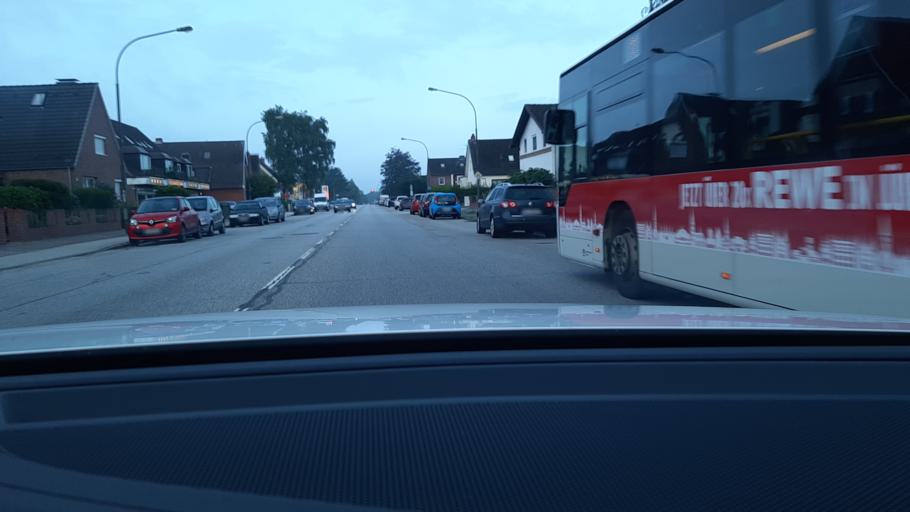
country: DE
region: Schleswig-Holstein
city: Stockelsdorf
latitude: 53.8612
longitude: 10.6489
